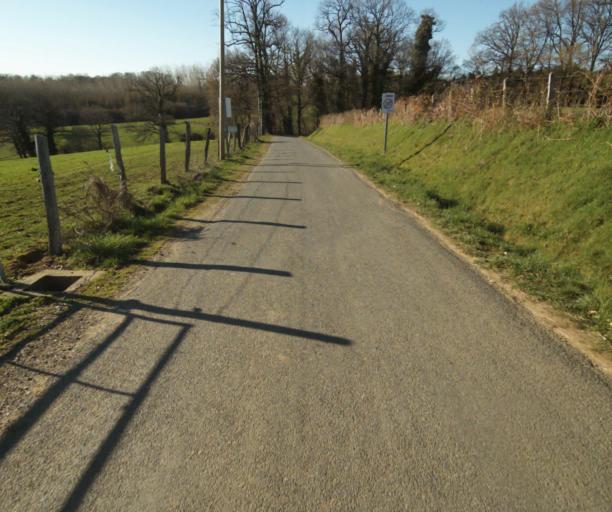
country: FR
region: Limousin
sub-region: Departement de la Correze
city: Seilhac
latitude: 45.3736
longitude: 1.7172
